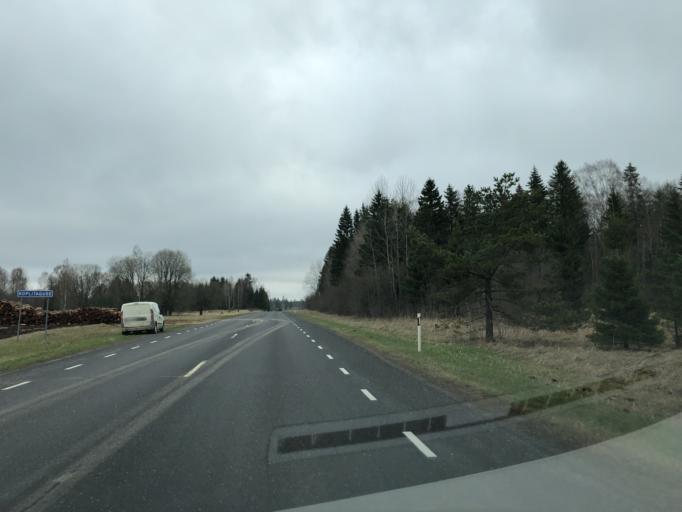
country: EE
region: Laeaene-Virumaa
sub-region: Vaeike-Maarja vald
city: Vaike-Maarja
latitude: 59.2408
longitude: 26.2688
